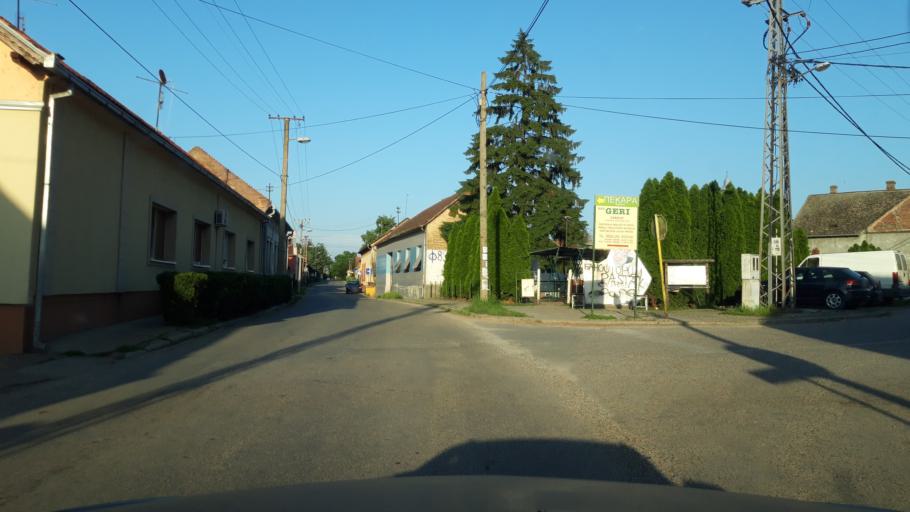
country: RS
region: Autonomna Pokrajina Vojvodina
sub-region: Juznobacki Okrug
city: Beocin
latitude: 45.2201
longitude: 19.6623
